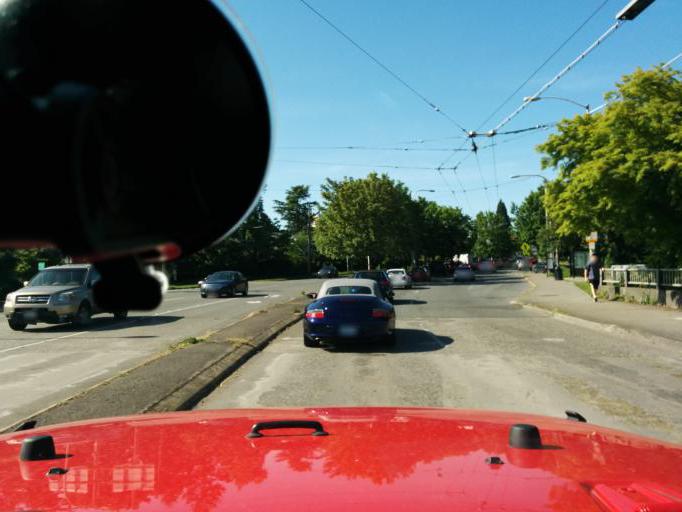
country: US
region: Washington
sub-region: King County
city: Seattle
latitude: 47.6443
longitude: -122.3044
